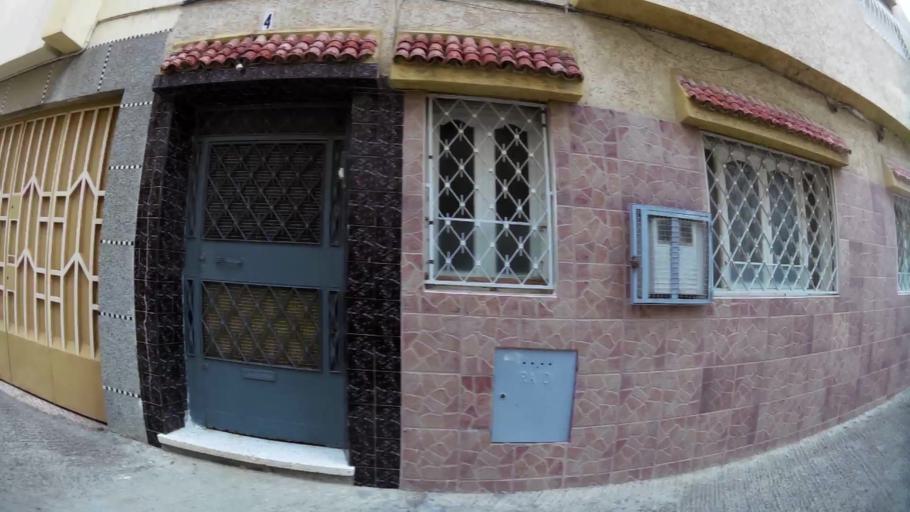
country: MA
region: Tanger-Tetouan
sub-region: Tanger-Assilah
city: Tangier
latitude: 35.7607
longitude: -5.8260
